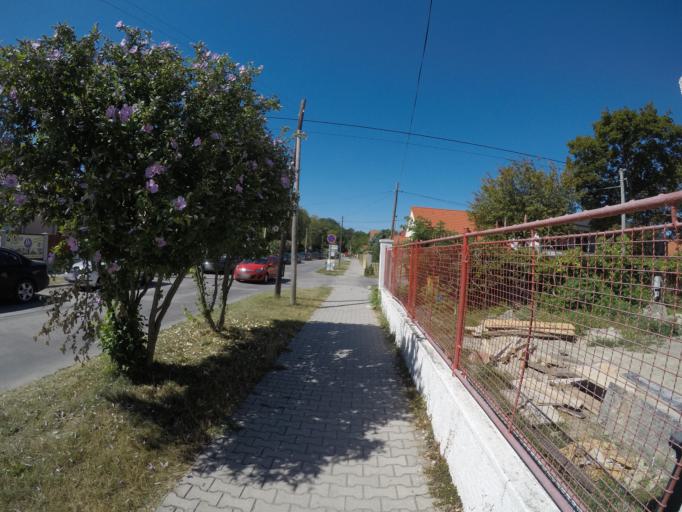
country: SK
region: Trnavsky
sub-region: Okres Dunajska Streda
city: Velky Meder
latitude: 47.8509
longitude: 17.7644
